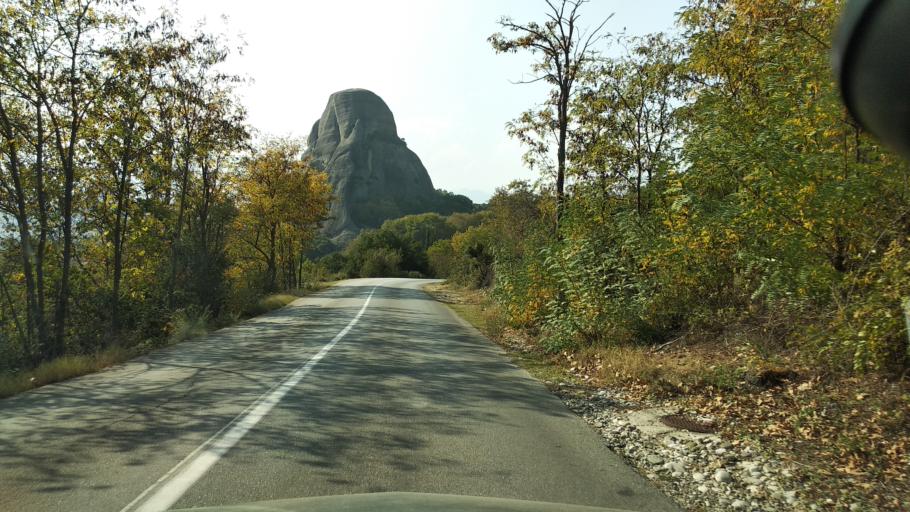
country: GR
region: Thessaly
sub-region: Trikala
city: Kastraki
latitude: 39.7227
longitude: 21.6268
